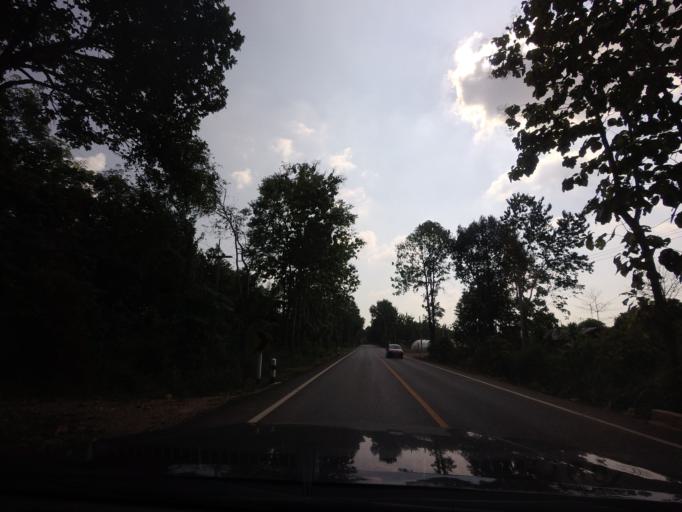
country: TH
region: Nan
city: Santi Suk
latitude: 18.9774
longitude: 100.9301
